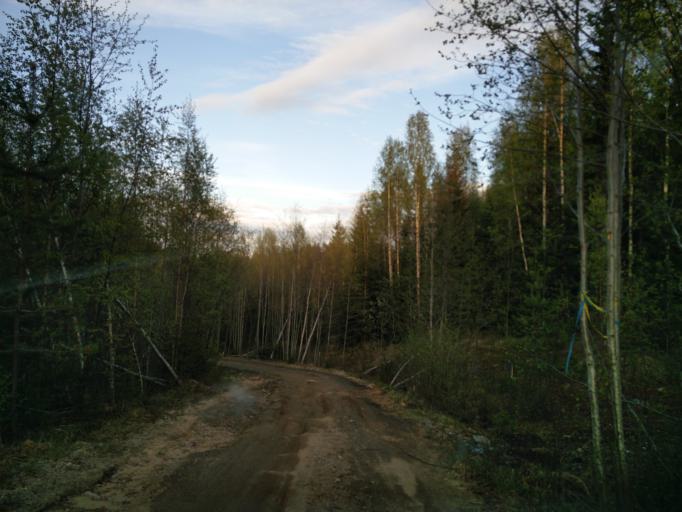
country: SE
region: Vaesternorrland
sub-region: Sundsvalls Kommun
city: Matfors
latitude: 62.3936
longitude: 16.8122
